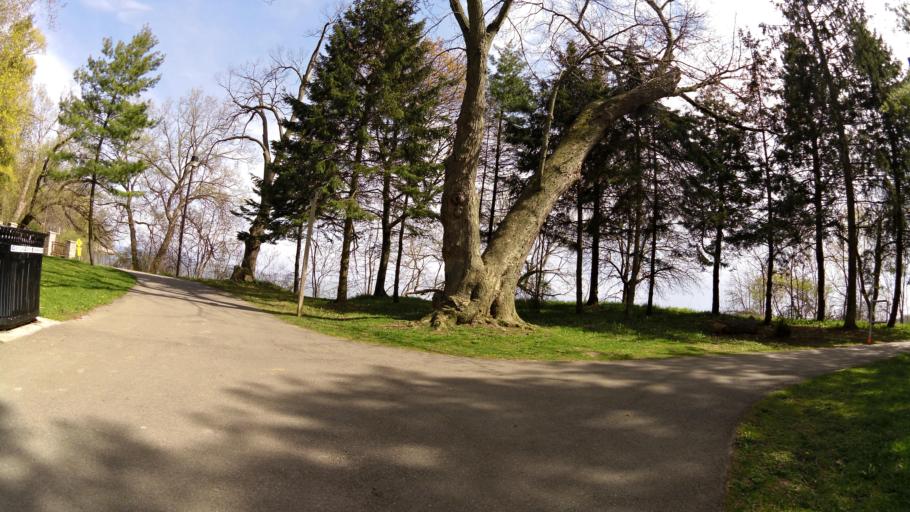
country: CA
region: Ontario
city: Mississauga
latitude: 43.5399
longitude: -79.5942
